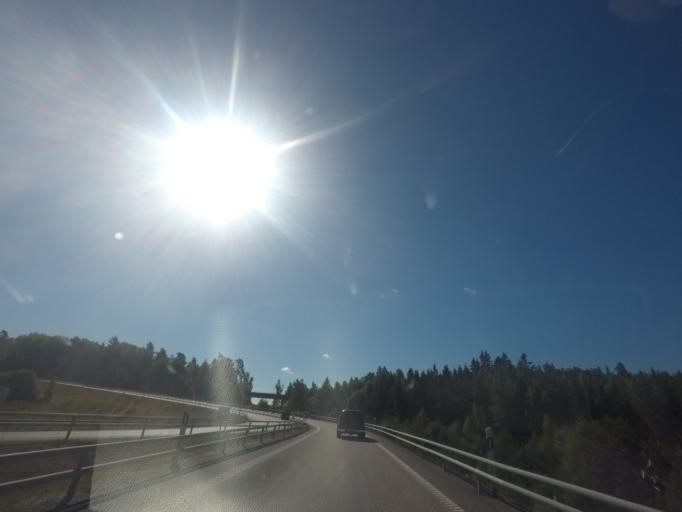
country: SE
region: Soedermanland
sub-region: Strangnas Kommun
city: Strangnas
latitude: 59.3671
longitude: 16.9502
